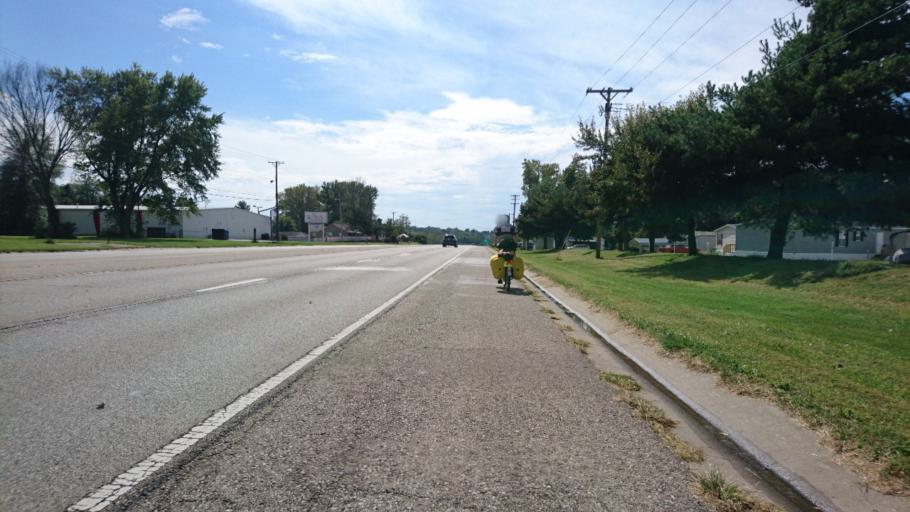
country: US
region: Illinois
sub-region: Sangamon County
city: Grandview
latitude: 39.8499
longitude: -89.6265
